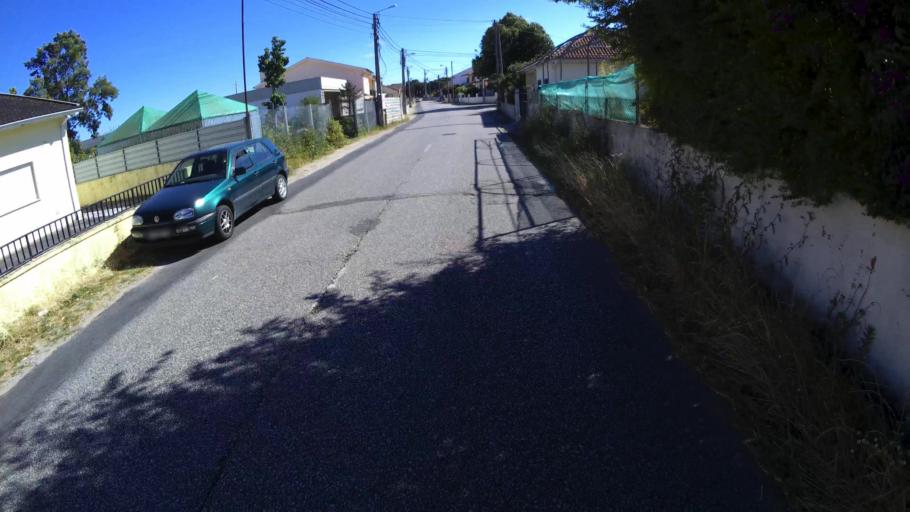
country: PT
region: Aveiro
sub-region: Aveiro
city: Aveiro
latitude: 40.6597
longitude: -8.6224
